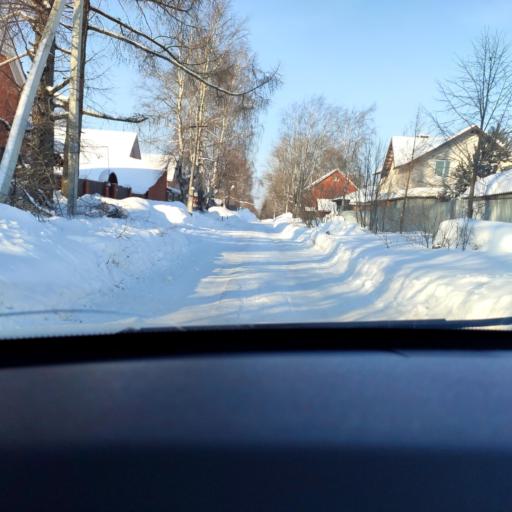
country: RU
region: Perm
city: Polazna
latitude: 58.1150
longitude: 56.4058
